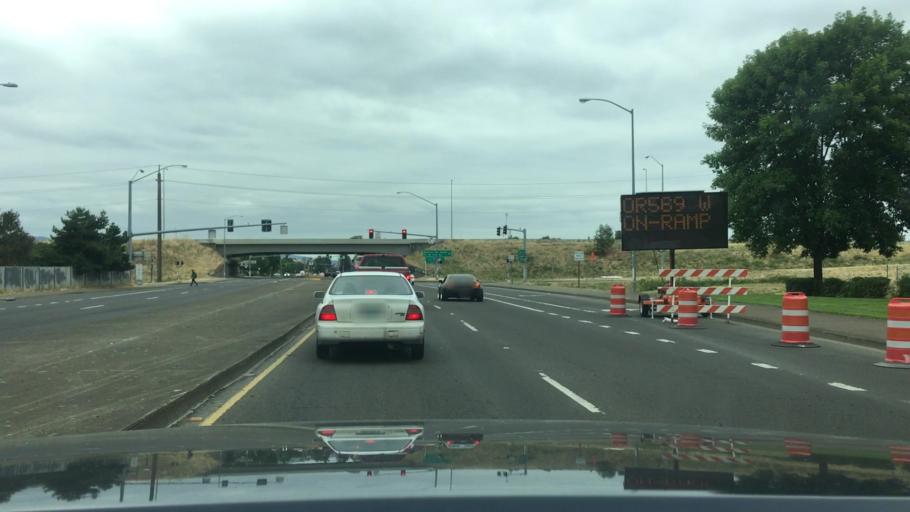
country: US
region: Oregon
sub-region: Lane County
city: Eugene
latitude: 44.0844
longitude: -123.1747
